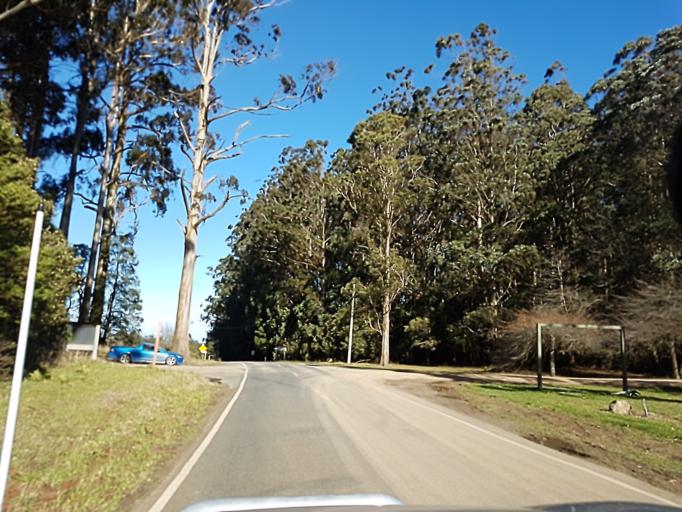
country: AU
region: Victoria
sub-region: Yarra Ranges
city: Healesville
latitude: -37.5668
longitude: 145.5086
